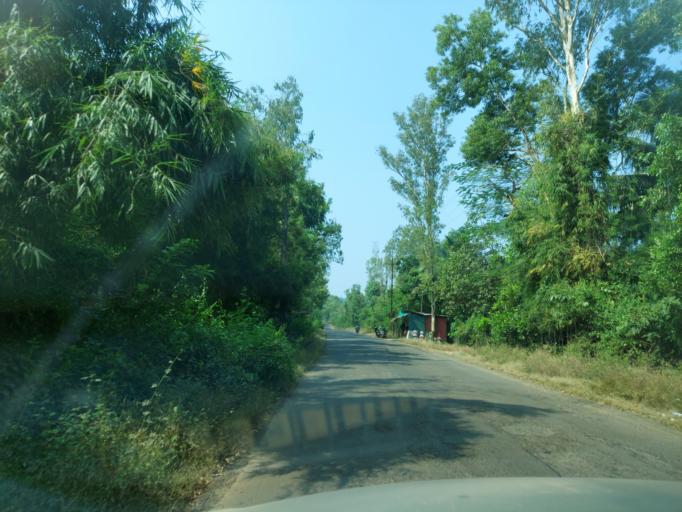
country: IN
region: Maharashtra
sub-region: Sindhudurg
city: Kudal
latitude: 15.9669
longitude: 73.5869
